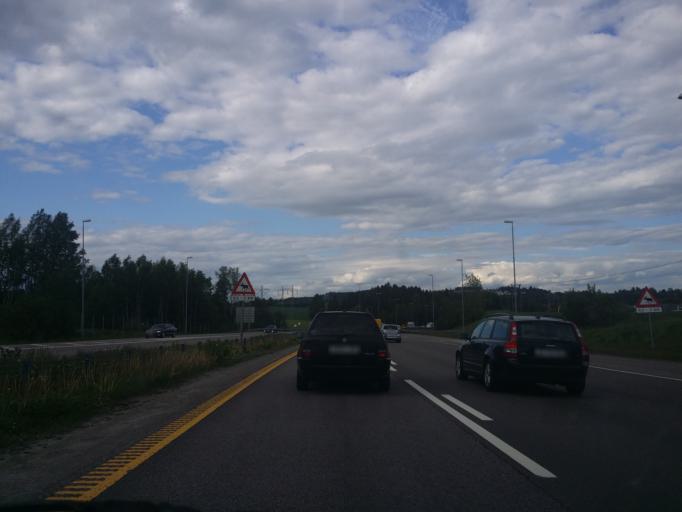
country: NO
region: Akershus
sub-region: Skedsmo
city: Lillestrom
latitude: 59.9805
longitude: 10.9958
